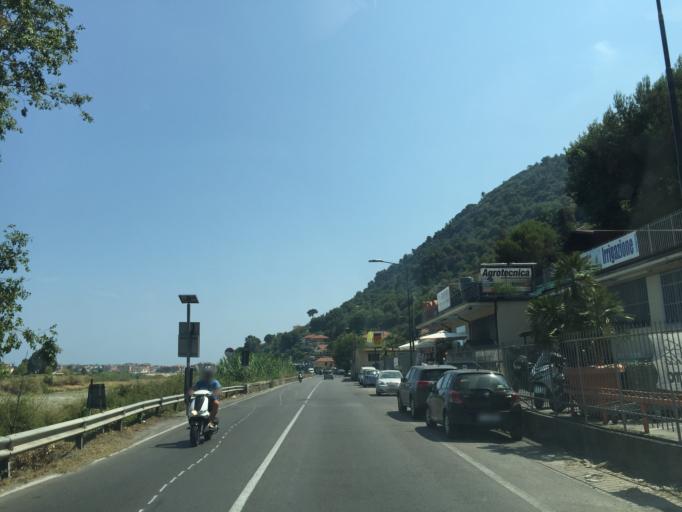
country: IT
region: Liguria
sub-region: Provincia di Imperia
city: Camporosso
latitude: 43.8006
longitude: 7.6256
